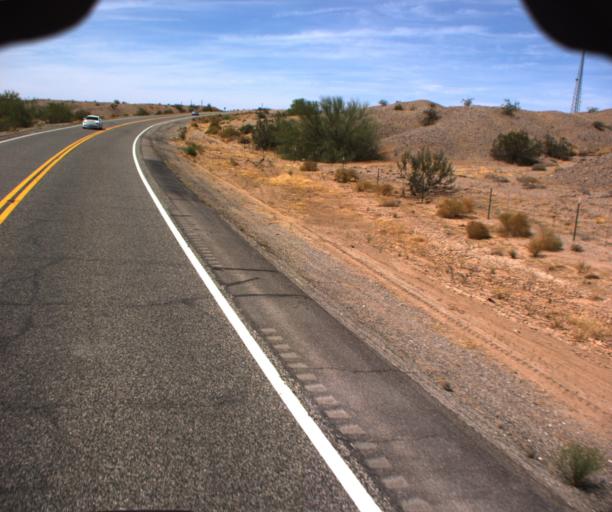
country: US
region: Arizona
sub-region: La Paz County
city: Parker
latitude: 33.9983
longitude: -114.2276
